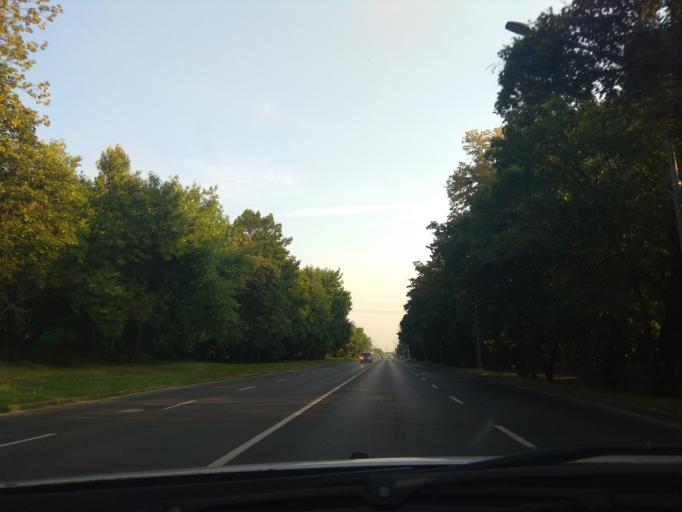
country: HU
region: Borsod-Abauj-Zemplen
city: Miskolc
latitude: 48.1224
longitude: 20.7868
